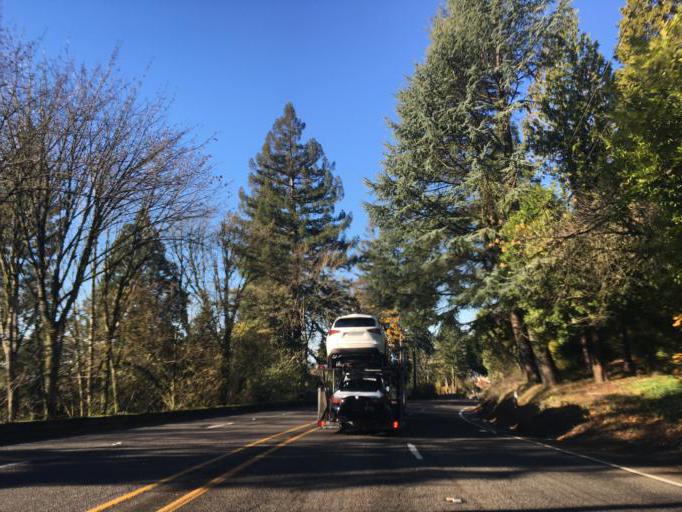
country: US
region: Oregon
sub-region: Washington County
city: West Slope
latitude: 45.4975
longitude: -122.7580
